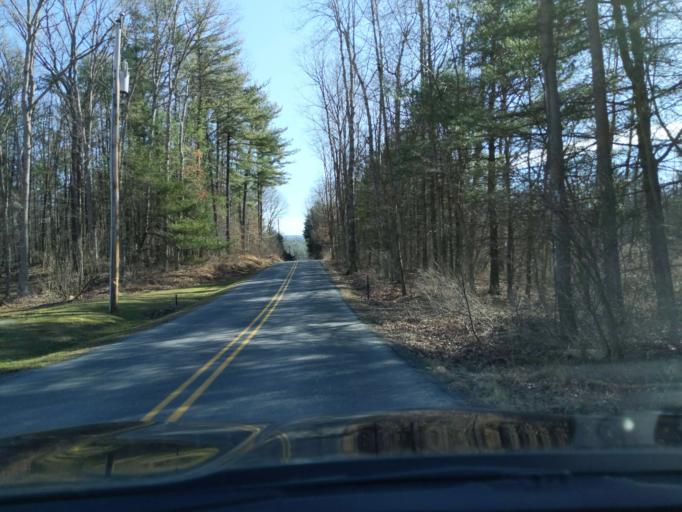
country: US
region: Pennsylvania
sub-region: Blair County
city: Martinsburg
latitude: 40.3771
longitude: -78.2569
